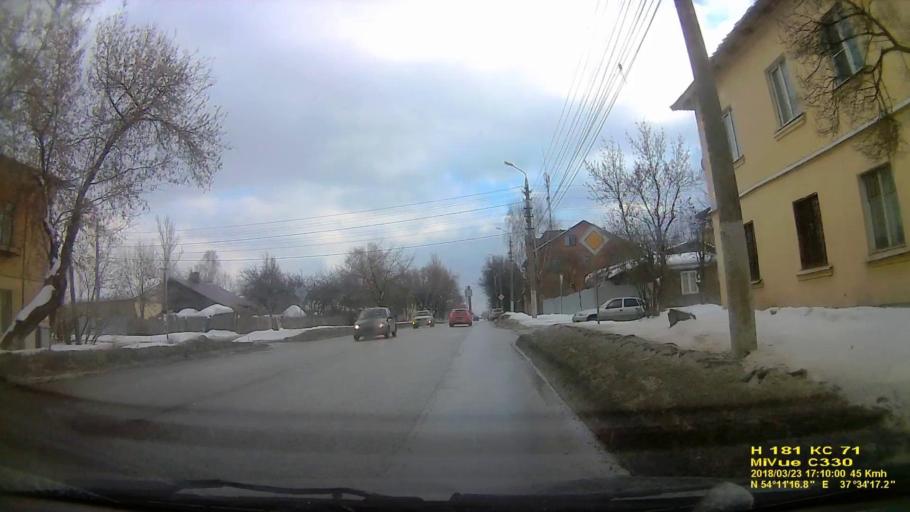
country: RU
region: Tula
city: Tula
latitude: 54.1881
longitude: 37.5723
